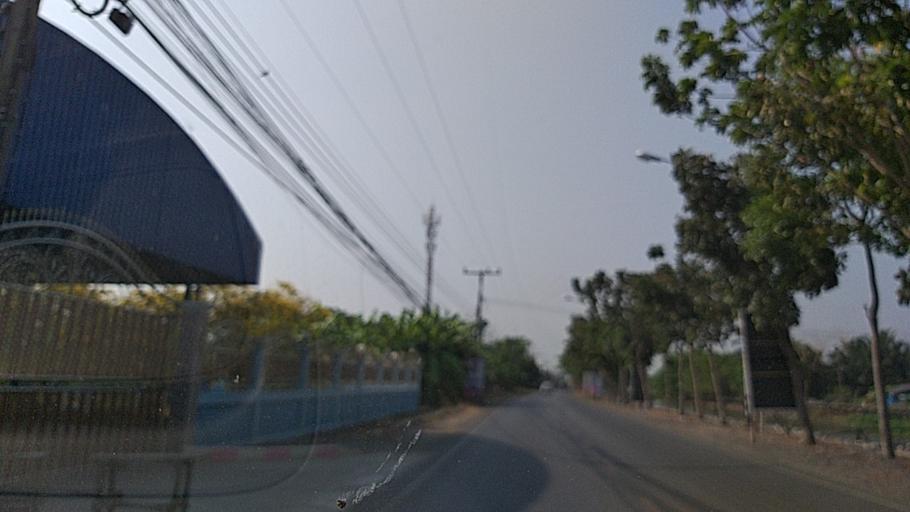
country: TH
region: Pathum Thani
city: Lam Luk Ka
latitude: 13.9452
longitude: 100.7060
